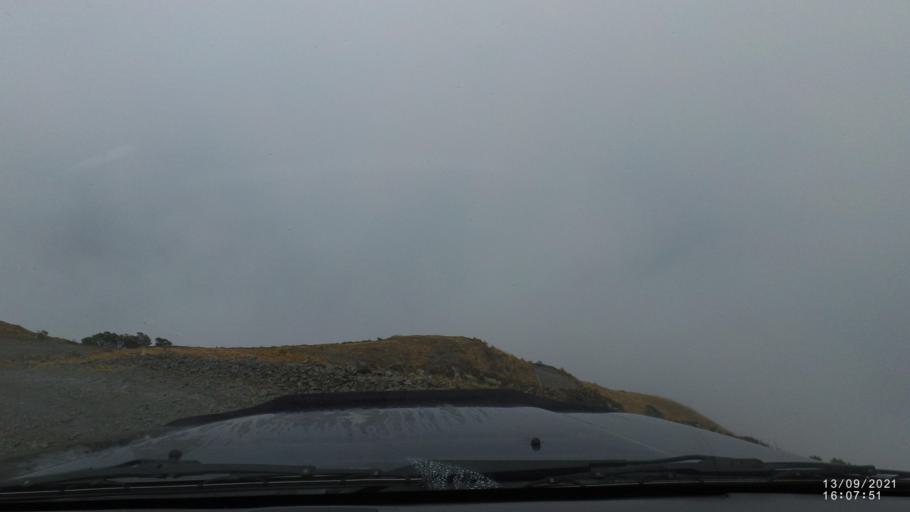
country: BO
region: Cochabamba
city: Colomi
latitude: -17.2784
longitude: -65.7083
